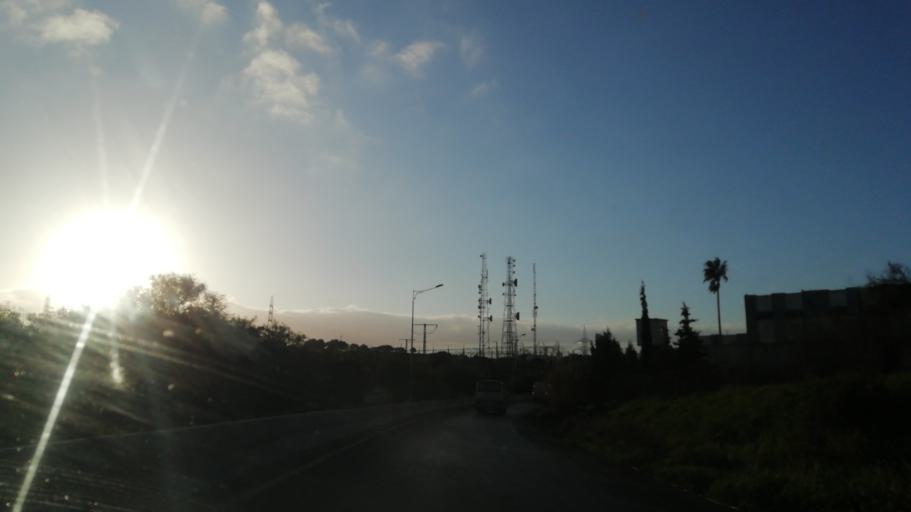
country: DZ
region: Oran
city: Oran
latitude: 35.6429
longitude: -0.7105
